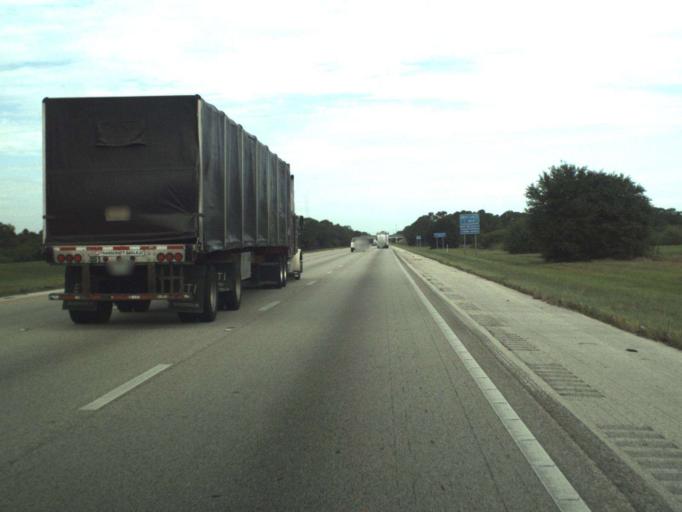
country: US
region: Florida
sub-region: Martin County
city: Palm City
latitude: 27.1274
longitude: -80.3100
